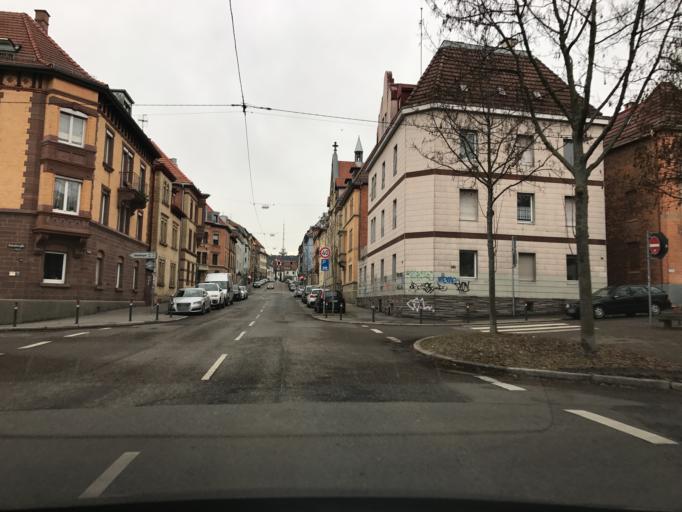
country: DE
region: Baden-Wuerttemberg
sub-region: Regierungsbezirk Stuttgart
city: Stuttgart-Ost
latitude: 48.7867
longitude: 9.2019
